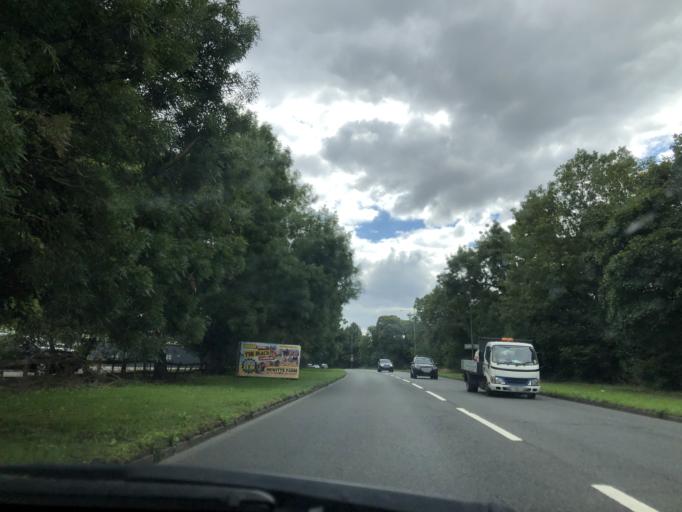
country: GB
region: England
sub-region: Kent
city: Halstead
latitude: 51.3505
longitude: 0.1303
